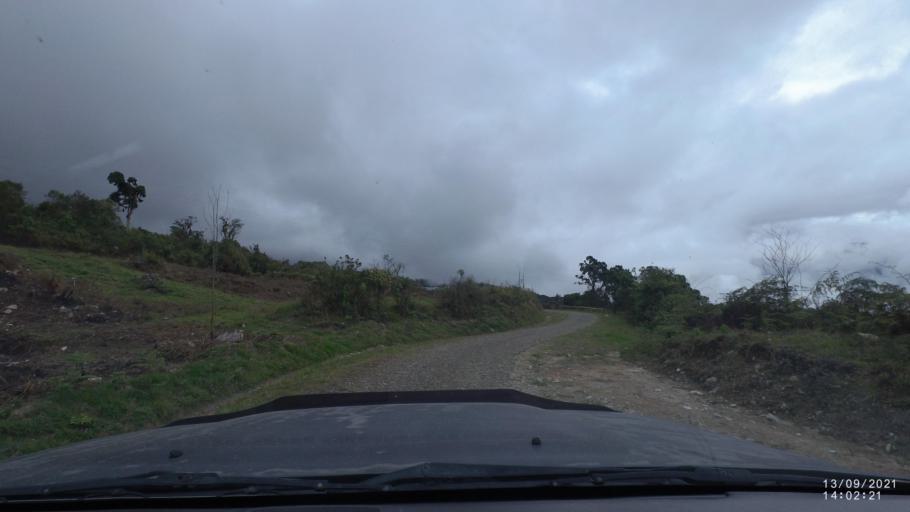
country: BO
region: Cochabamba
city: Colomi
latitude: -17.2088
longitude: -65.8670
